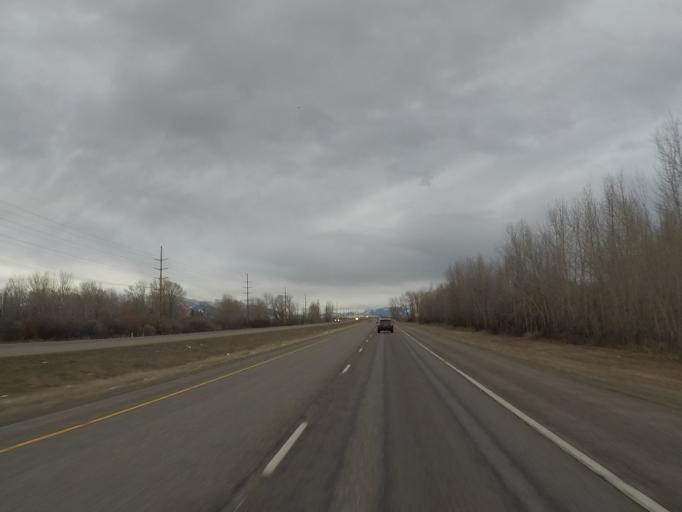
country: US
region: Montana
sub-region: Gallatin County
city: Manhattan
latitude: 45.8261
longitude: -111.2768
